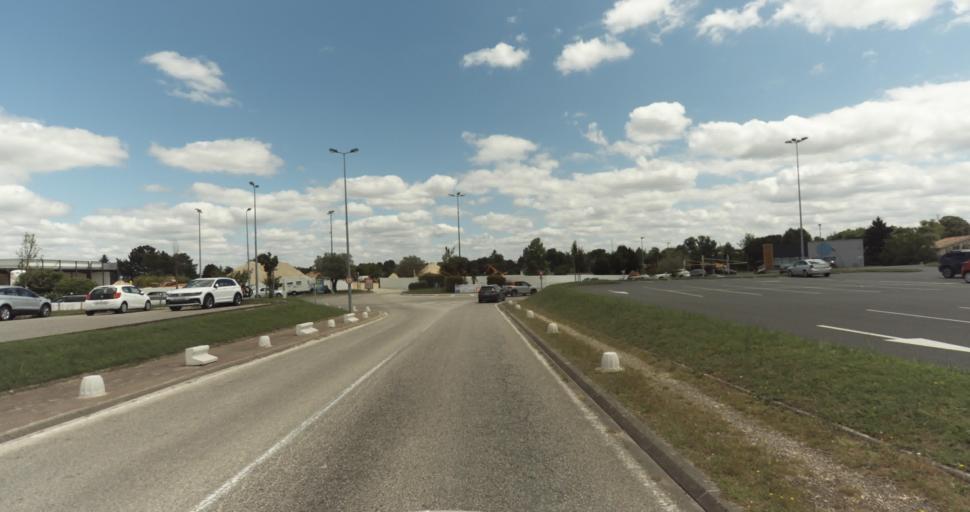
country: FR
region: Aquitaine
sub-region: Departement de la Gironde
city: Langon
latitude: 44.5428
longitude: -0.2528
